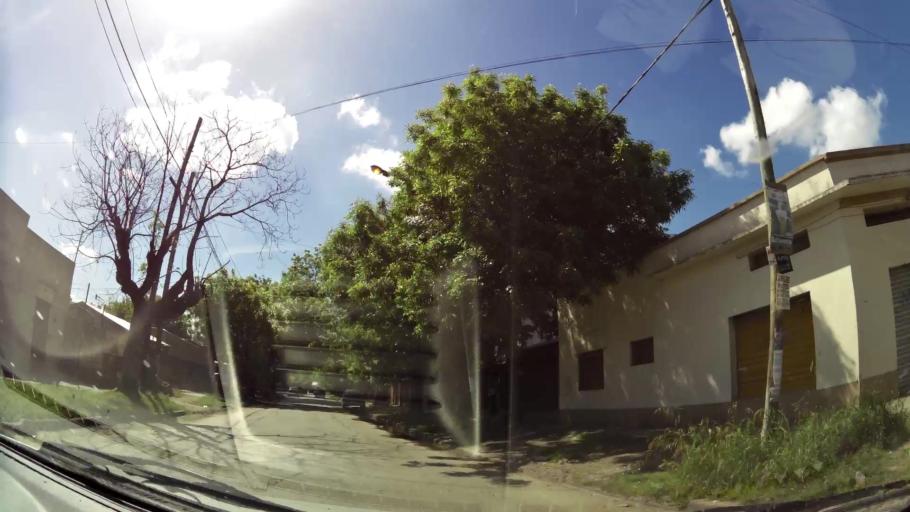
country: AR
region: Buenos Aires
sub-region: Partido de Quilmes
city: Quilmes
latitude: -34.8130
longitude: -58.2603
